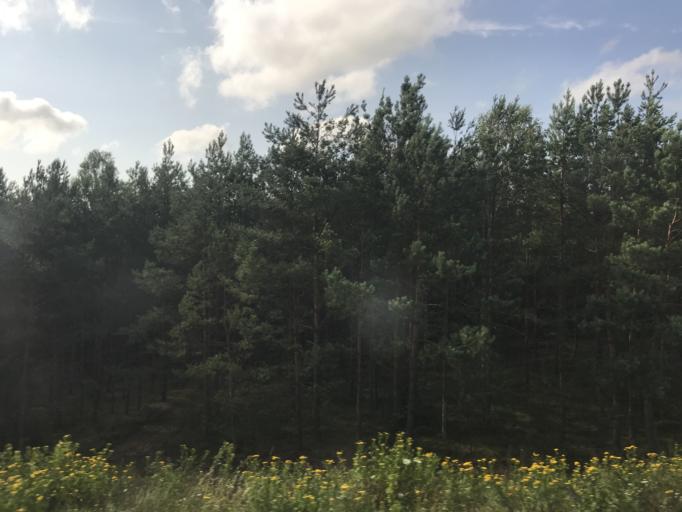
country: PL
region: Kujawsko-Pomorskie
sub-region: Powiat swiecki
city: Warlubie
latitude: 53.5595
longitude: 18.5651
